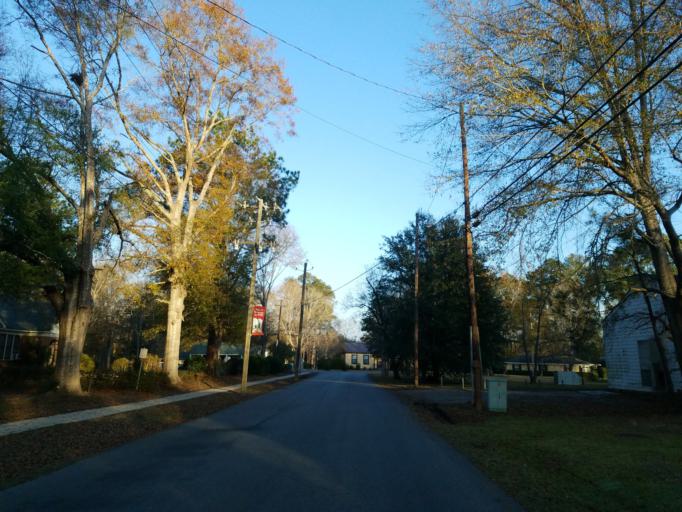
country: US
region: Mississippi
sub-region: Clarke County
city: Stonewall
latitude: 32.1743
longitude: -88.8222
